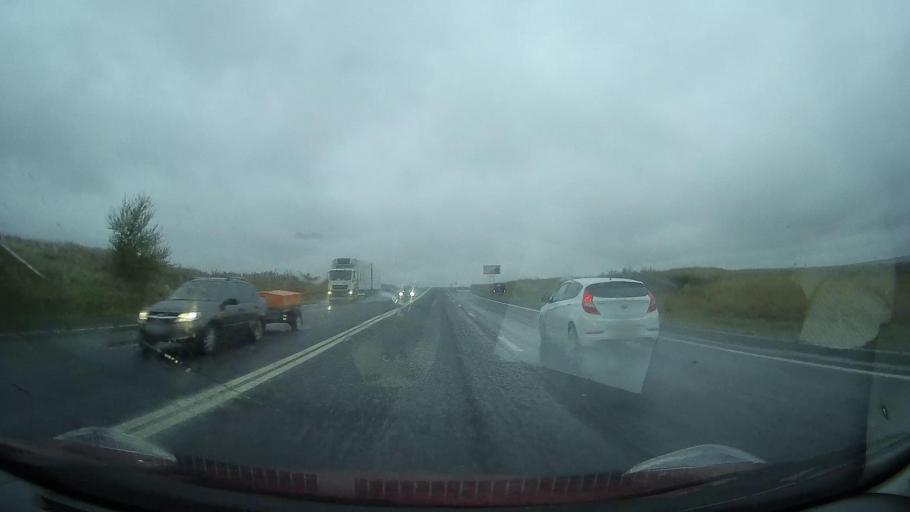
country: RU
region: Stavropol'skiy
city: Nevinnomyssk
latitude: 44.6238
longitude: 42.0688
